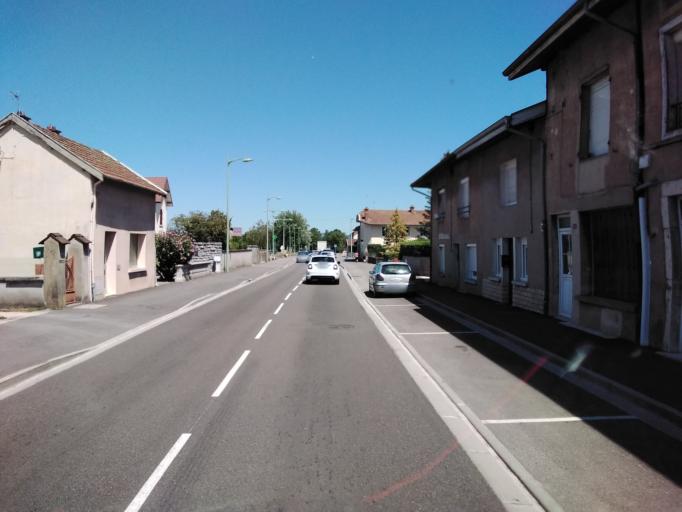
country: FR
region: Rhone-Alpes
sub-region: Departement de l'Ain
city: Saint-Etienne-du-Bois
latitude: 46.2889
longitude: 5.2948
